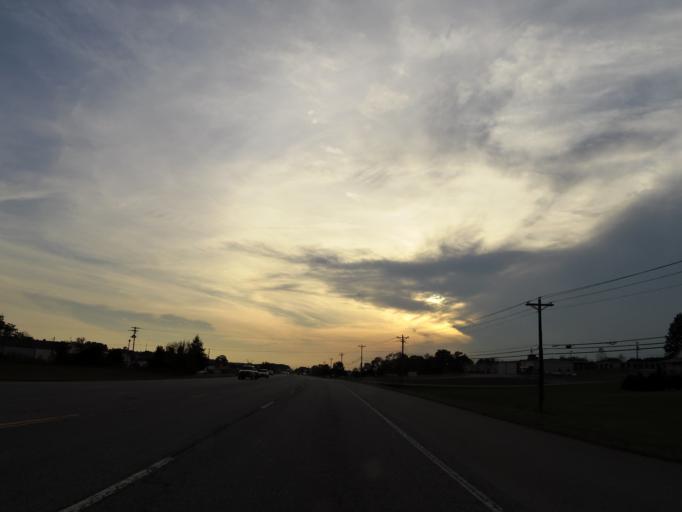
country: US
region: Tennessee
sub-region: Loudon County
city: Greenback
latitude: 35.6712
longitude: -84.0902
